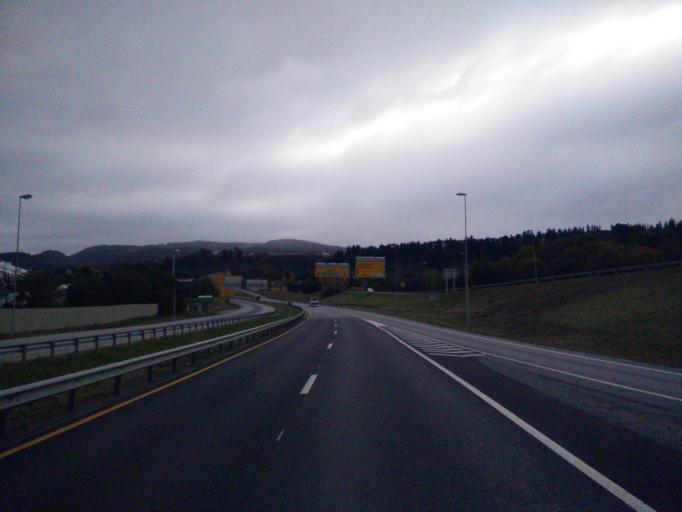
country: NO
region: Sor-Trondelag
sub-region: Trondheim
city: Trondheim
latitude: 63.4241
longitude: 10.5201
